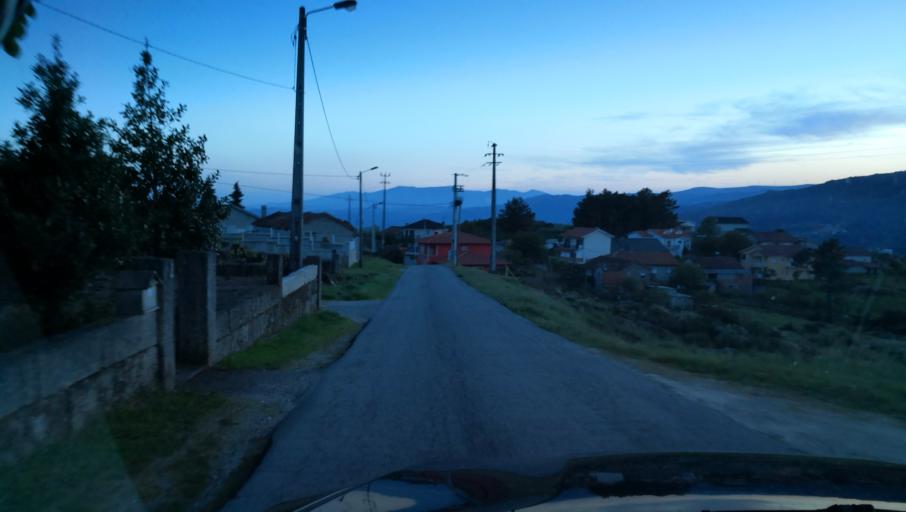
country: PT
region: Vila Real
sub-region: Vila Real
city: Vila Real
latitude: 41.3507
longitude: -7.6837
